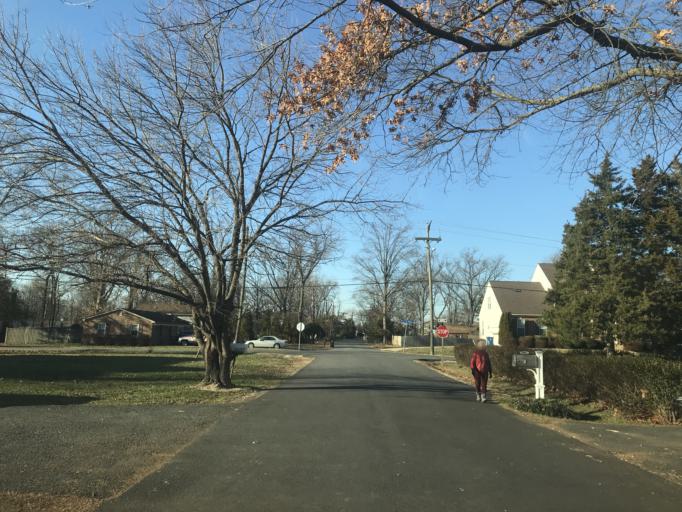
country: US
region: Virginia
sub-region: Fairfax County
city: Franconia
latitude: 38.7908
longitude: -77.1500
